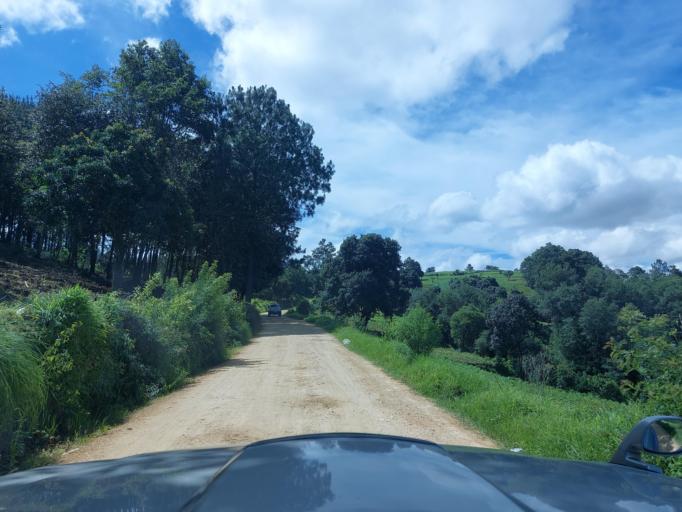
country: GT
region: Chimaltenango
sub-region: Municipio de San Juan Comalapa
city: Comalapa
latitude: 14.7595
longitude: -90.8792
